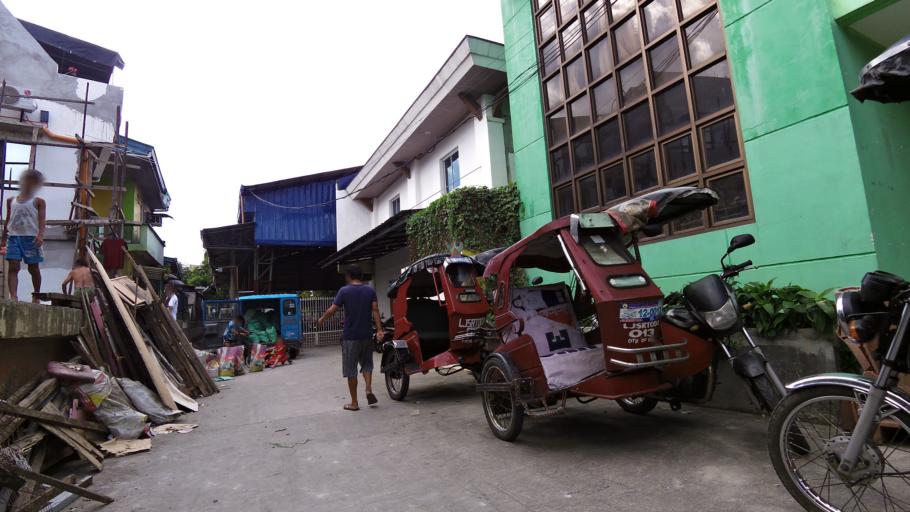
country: PH
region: Calabarzon
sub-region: Province of Rizal
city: Pateros
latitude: 14.5610
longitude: 121.0733
